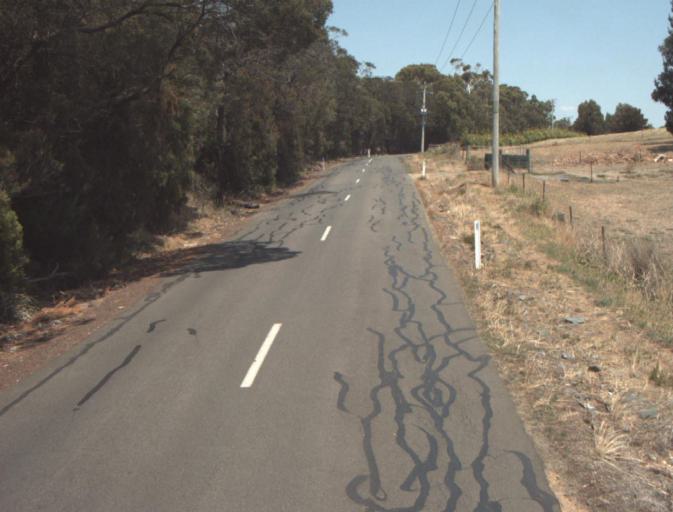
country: AU
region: Tasmania
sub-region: Launceston
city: Newstead
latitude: -41.4951
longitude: 147.2088
